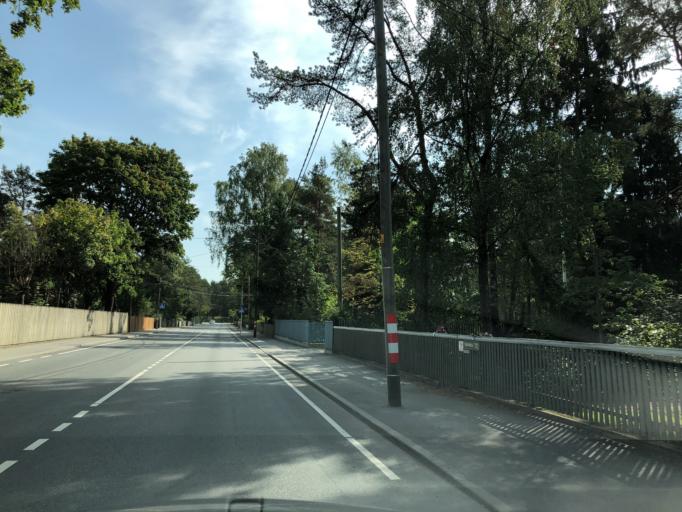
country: EE
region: Harju
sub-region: Tallinna linn
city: Tallinn
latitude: 59.3799
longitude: 24.7009
